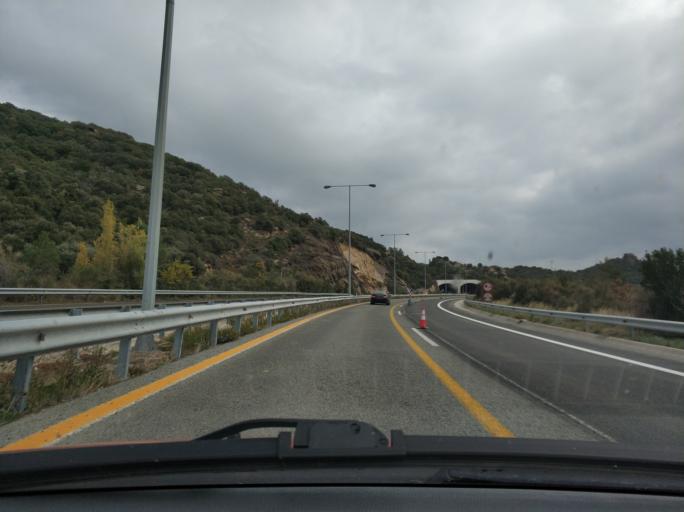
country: GR
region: East Macedonia and Thrace
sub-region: Nomos Kavalas
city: Palaio Tsifliki
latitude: 40.9102
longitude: 24.3518
